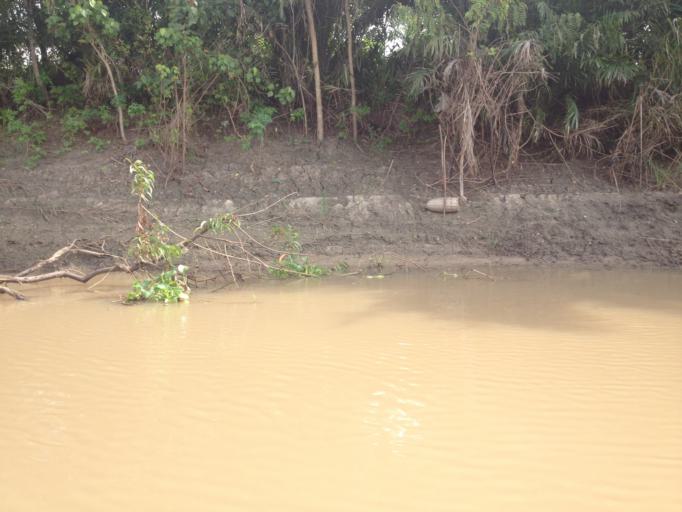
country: BJ
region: Mono
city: Come
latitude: 6.3831
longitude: 1.7848
